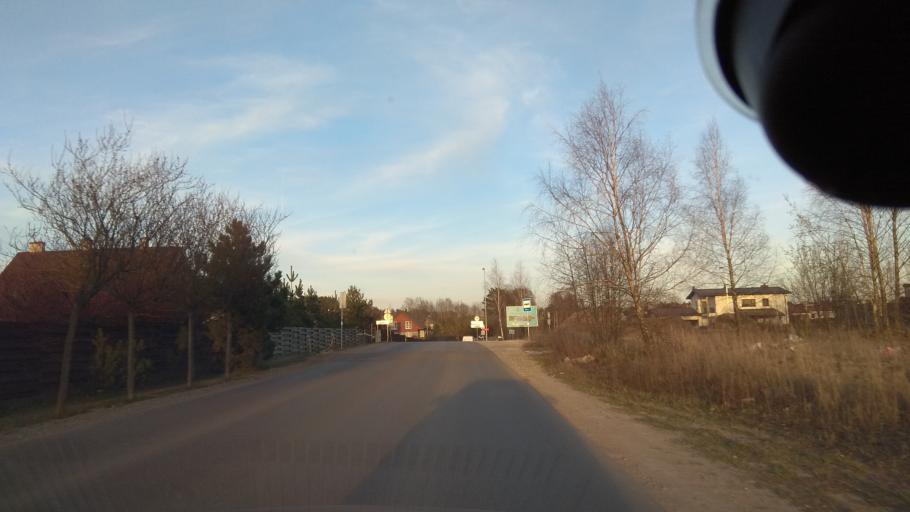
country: LT
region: Vilnius County
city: Pasilaiciai
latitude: 54.7577
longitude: 25.2284
